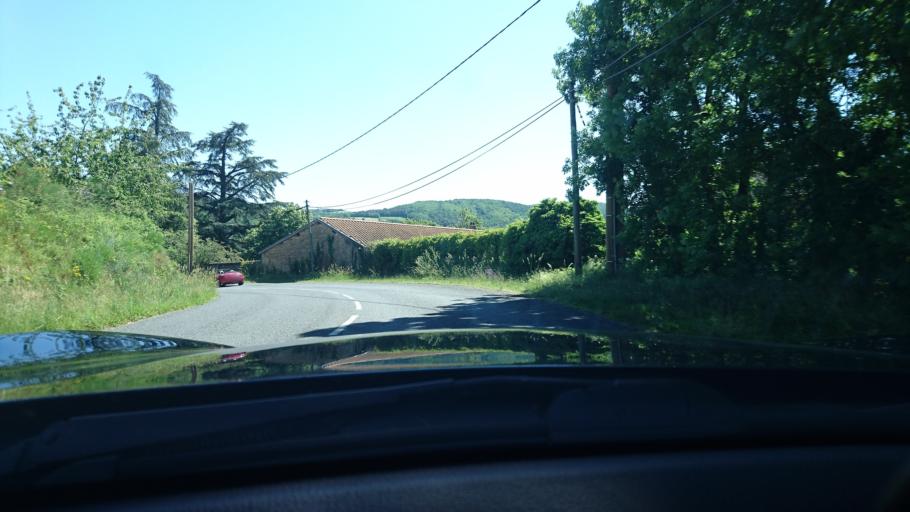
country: FR
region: Rhone-Alpes
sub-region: Departement du Rhone
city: Vaugneray
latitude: 45.7250
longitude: 4.6417
